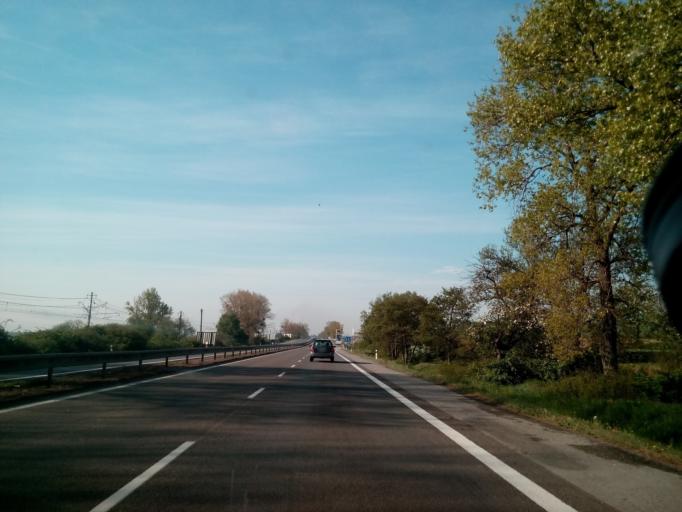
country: SK
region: Kosicky
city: Kosice
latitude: 48.6684
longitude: 21.2099
